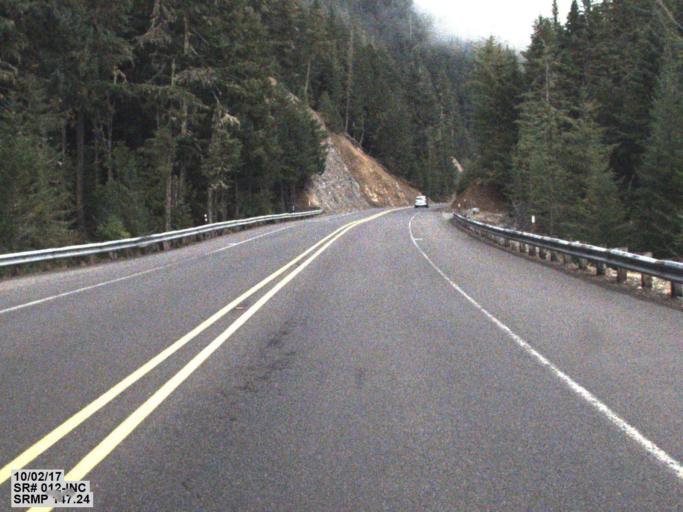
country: US
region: Washington
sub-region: Yakima County
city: Tieton
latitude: 46.6372
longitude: -121.4508
